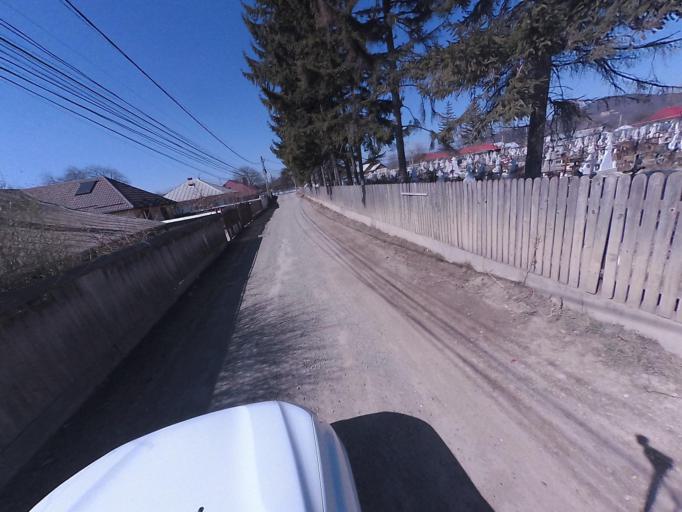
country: RO
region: Neamt
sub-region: Oras Targu Neamt
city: Humulesti
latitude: 47.1942
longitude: 26.3475
